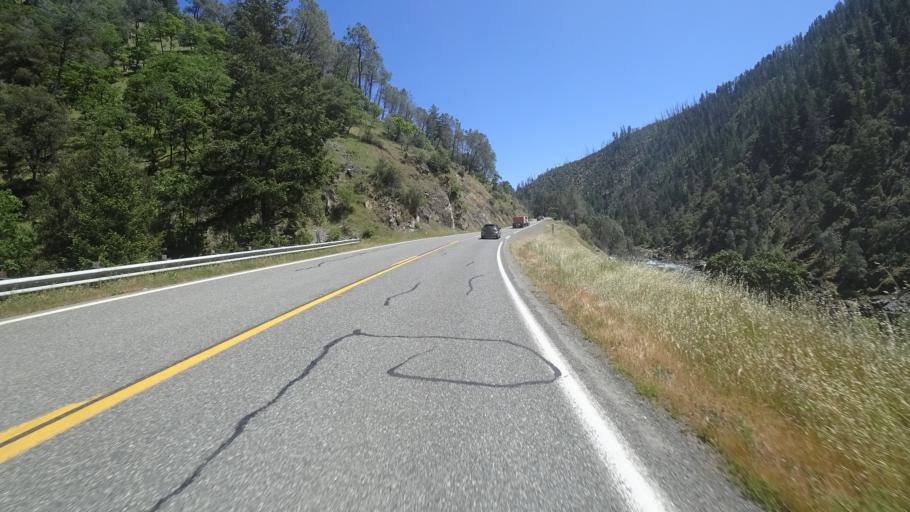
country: US
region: California
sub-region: Trinity County
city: Hayfork
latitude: 40.7953
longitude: -123.3644
